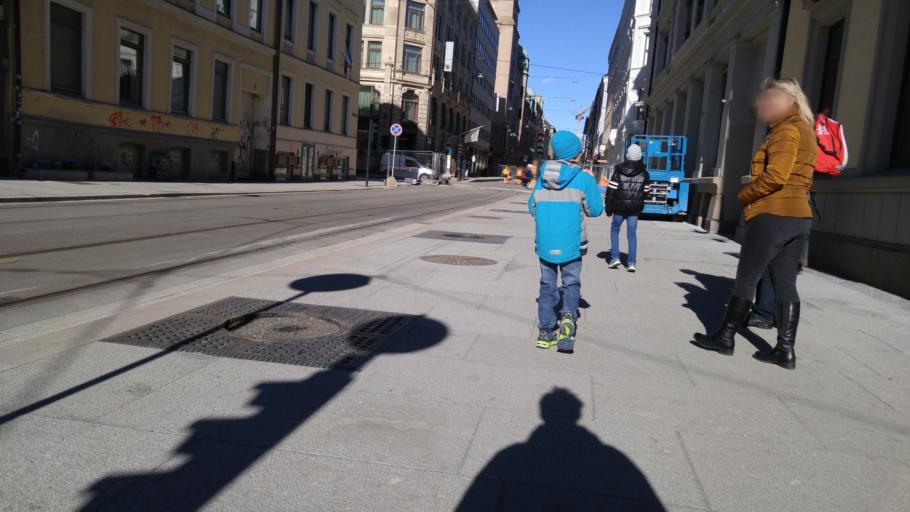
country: NO
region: Oslo
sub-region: Oslo
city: Oslo
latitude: 59.9103
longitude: 10.7483
